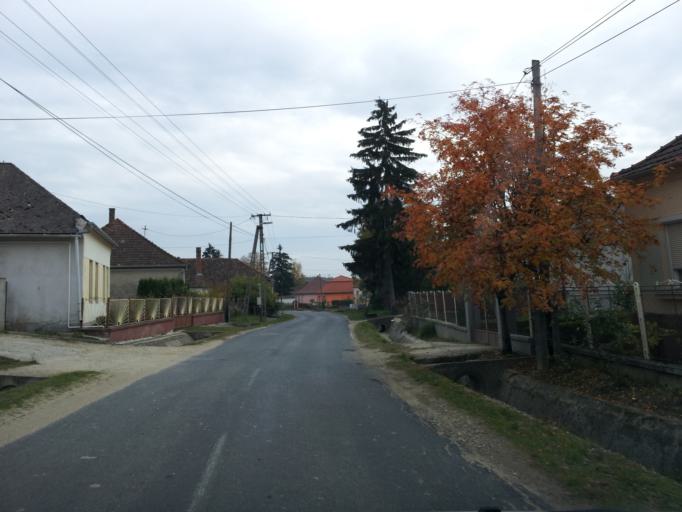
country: HU
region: Gyor-Moson-Sopron
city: Pannonhalma
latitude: 47.4791
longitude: 17.7030
